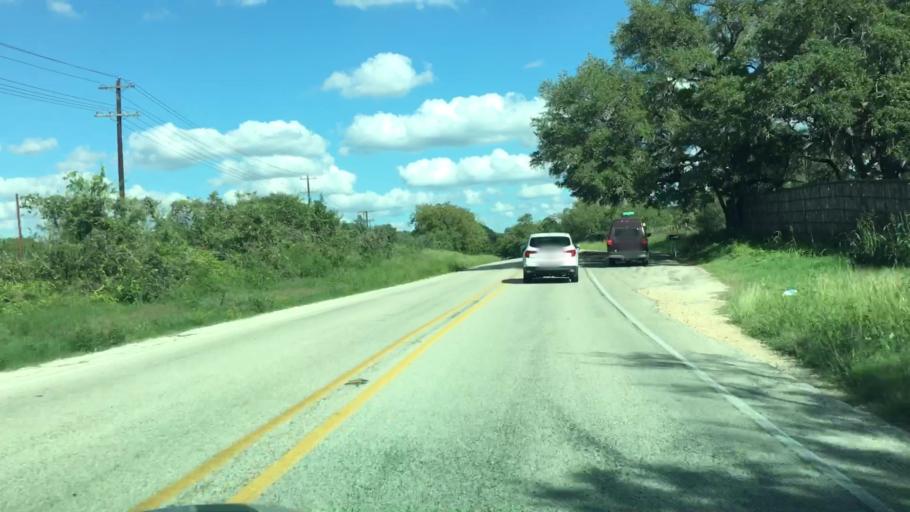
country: US
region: Texas
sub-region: Blanco County
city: Blanco
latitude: 30.0916
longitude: -98.3789
